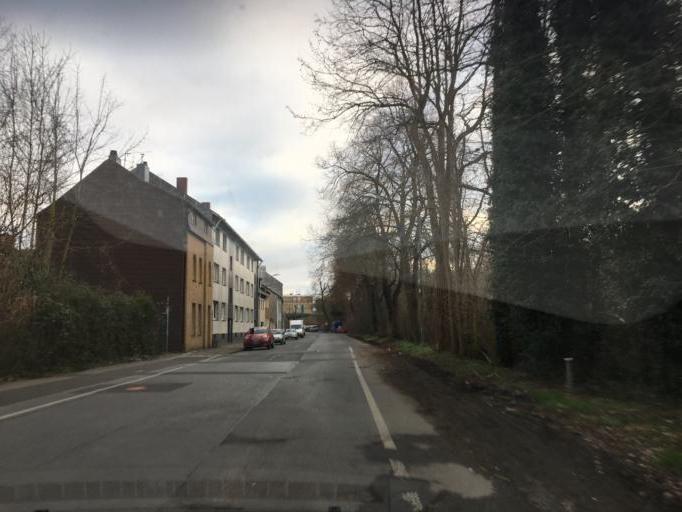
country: DE
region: North Rhine-Westphalia
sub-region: Regierungsbezirk Koln
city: Dueren
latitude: 50.8034
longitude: 6.4682
